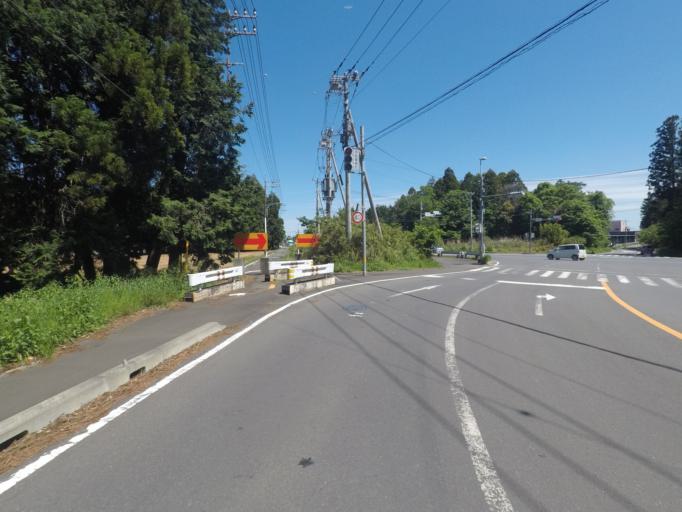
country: JP
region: Ibaraki
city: Ami
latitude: 36.0968
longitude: 140.2503
